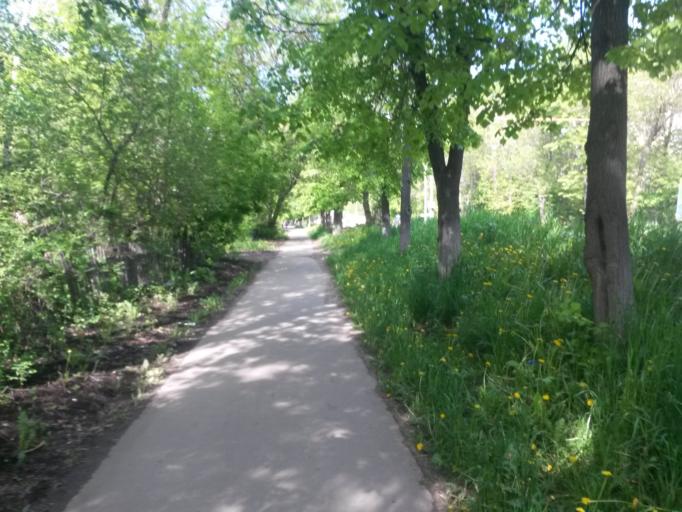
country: RU
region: Ivanovo
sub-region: Gorod Ivanovo
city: Ivanovo
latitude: 57.0051
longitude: 40.9473
